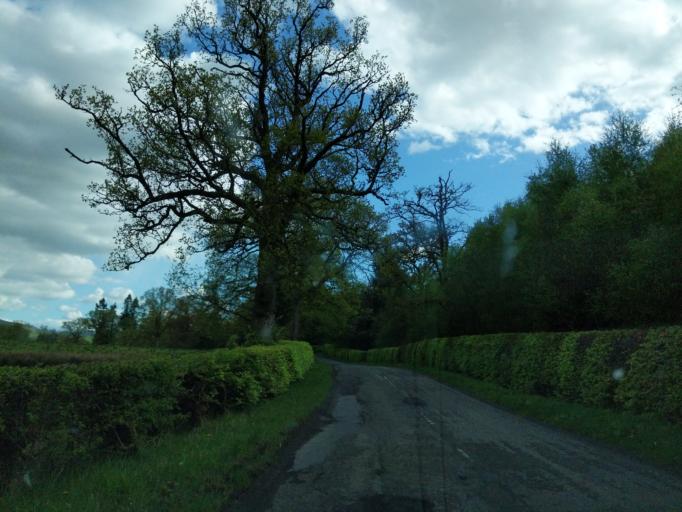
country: GB
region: Scotland
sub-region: Stirling
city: Callander
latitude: 56.1574
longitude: -4.2626
